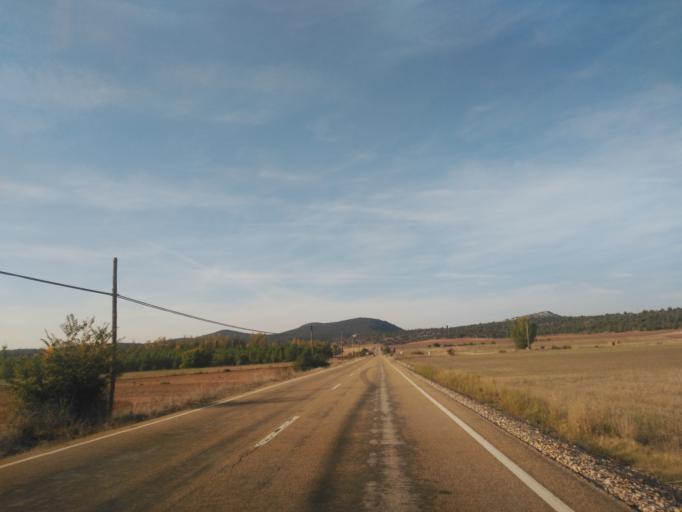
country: ES
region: Castille and Leon
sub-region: Provincia de Soria
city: Ucero
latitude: 41.7002
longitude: -3.0442
